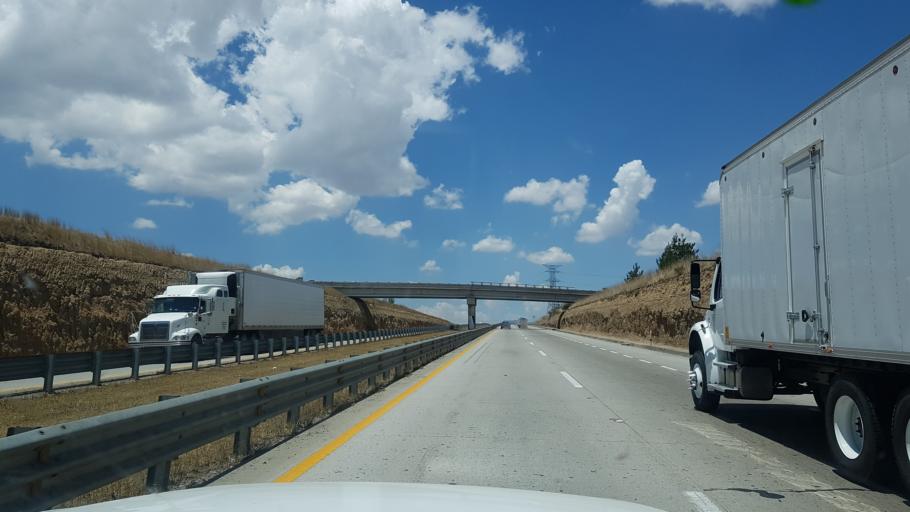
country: MX
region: Hidalgo
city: Calpulalpan
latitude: 19.5812
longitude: -98.5143
